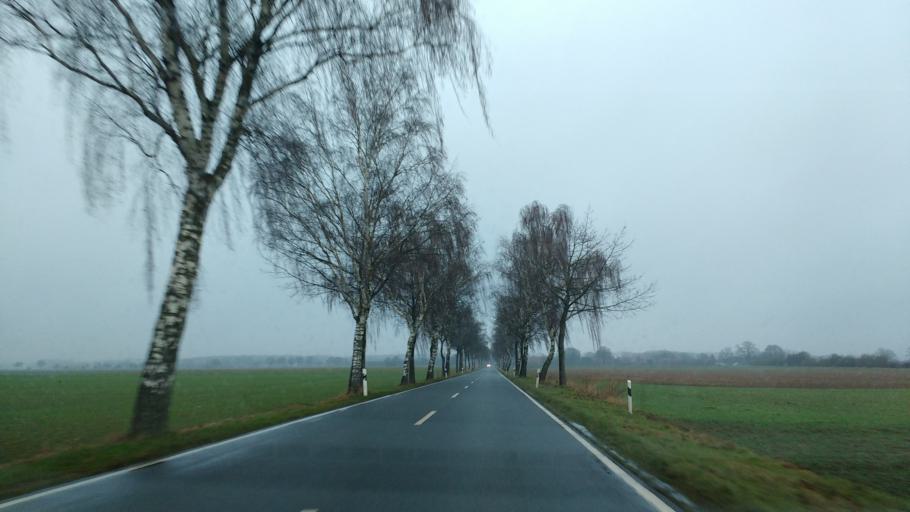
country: DE
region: Lower Saxony
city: Gilten
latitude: 52.6553
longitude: 9.5738
